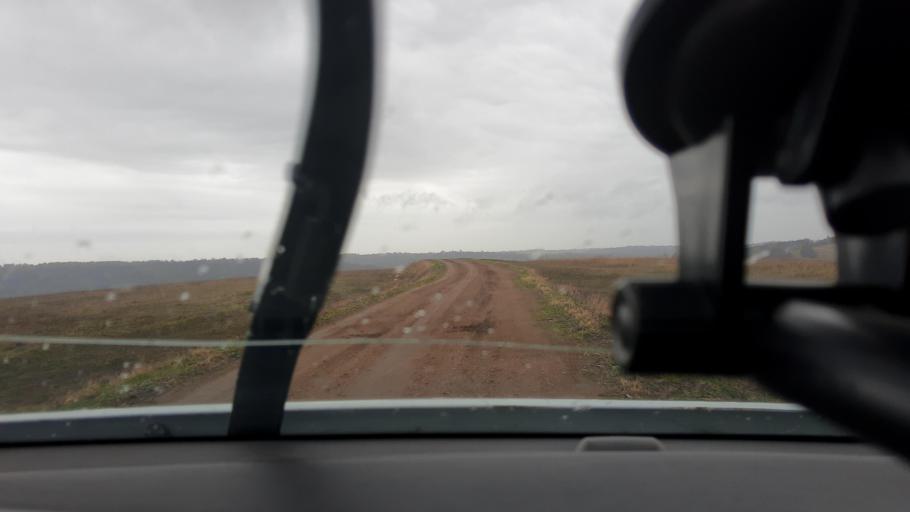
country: RU
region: Bashkortostan
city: Pavlovka
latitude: 55.4300
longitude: 56.3206
